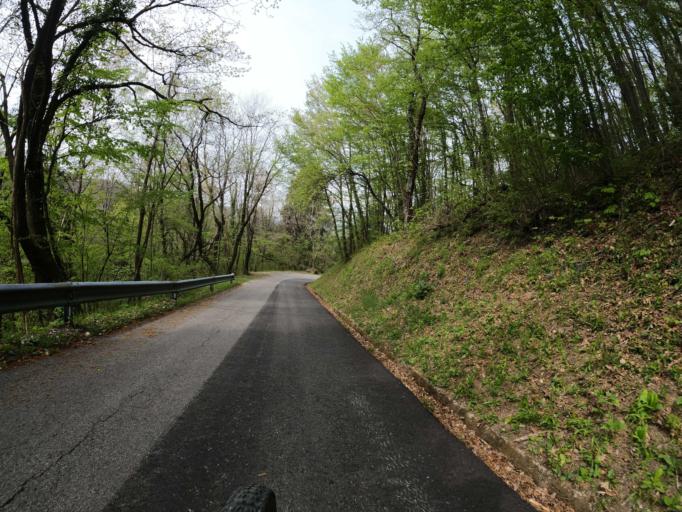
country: IT
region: Friuli Venezia Giulia
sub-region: Provincia di Udine
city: Cras
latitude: 46.1471
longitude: 13.6231
